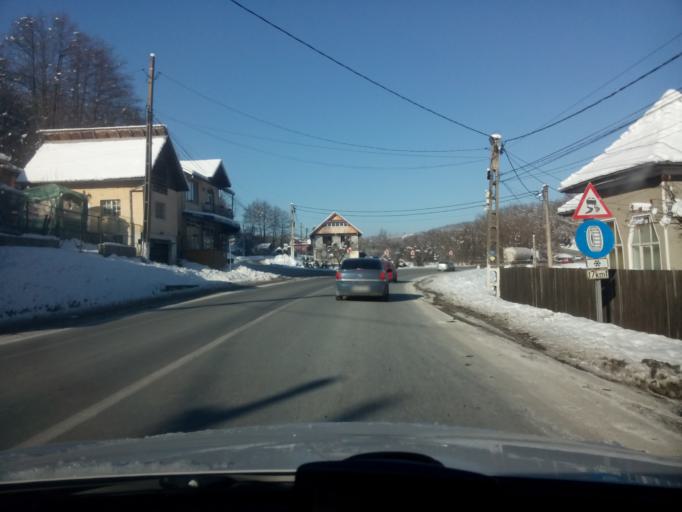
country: RO
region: Valcea
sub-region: Comuna Milcoiu
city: Milcoiu
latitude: 45.0327
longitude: 24.4761
